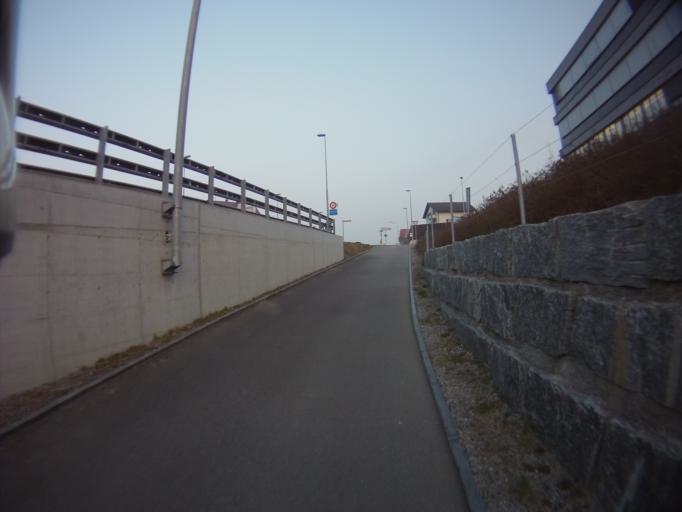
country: CH
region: Zug
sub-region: Zug
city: Cham
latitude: 47.1915
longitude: 8.4468
